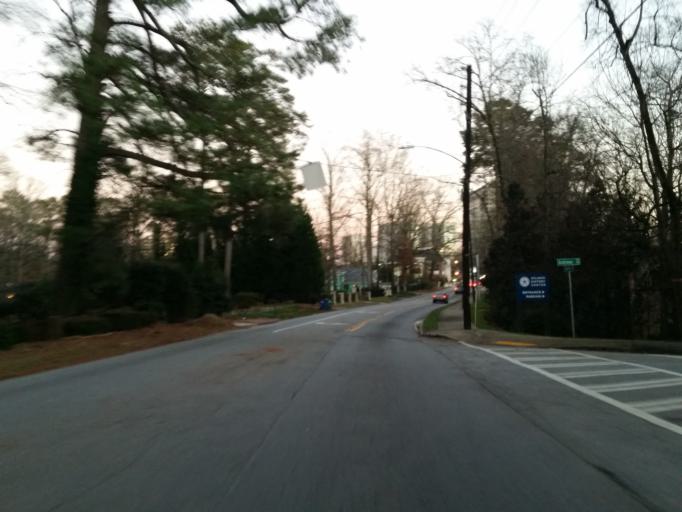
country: US
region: Georgia
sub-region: DeKalb County
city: North Atlanta
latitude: 33.8437
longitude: -84.3877
